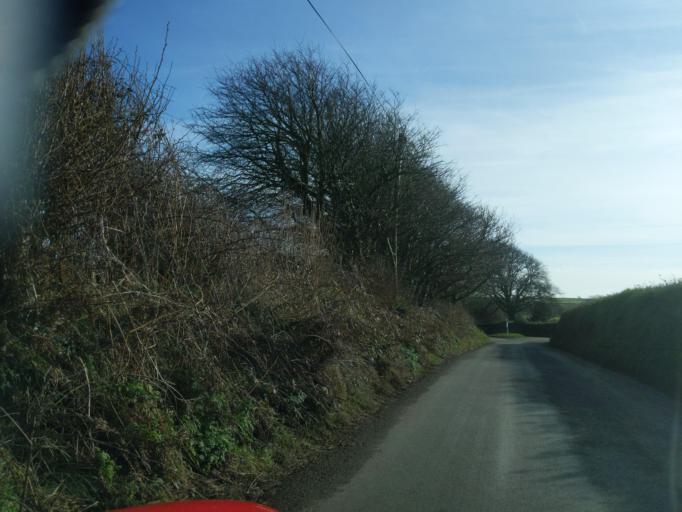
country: GB
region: England
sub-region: Devon
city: Kingsbridge
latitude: 50.3282
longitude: -3.7178
